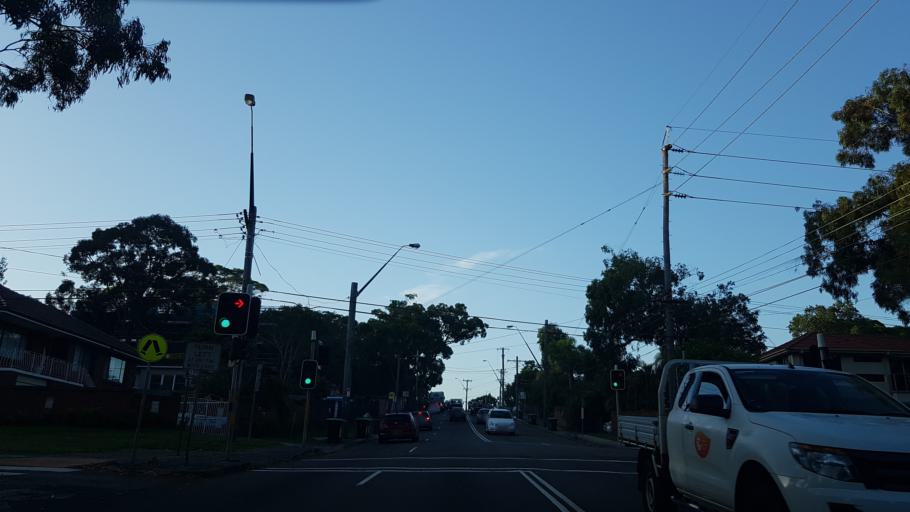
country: AU
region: New South Wales
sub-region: Warringah
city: Narraweena
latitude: -33.7520
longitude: 151.2614
